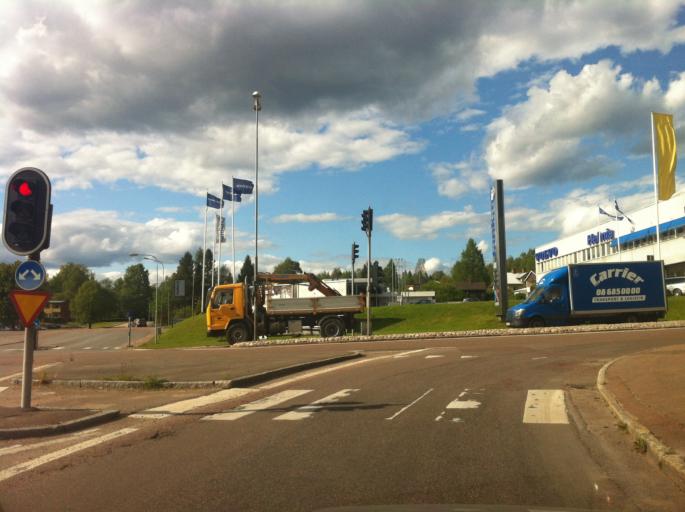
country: SE
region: Vaermland
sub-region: Filipstads Kommun
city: Filipstad
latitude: 59.7015
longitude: 14.1826
